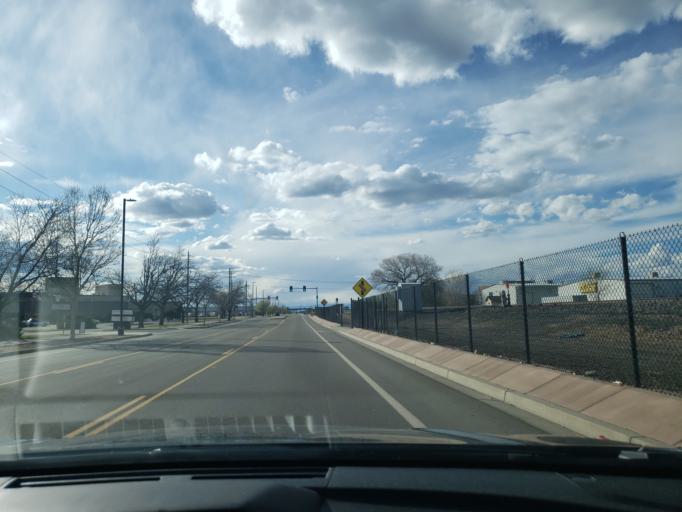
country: US
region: Colorado
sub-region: Mesa County
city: Redlands
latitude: 39.0847
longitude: -108.5969
